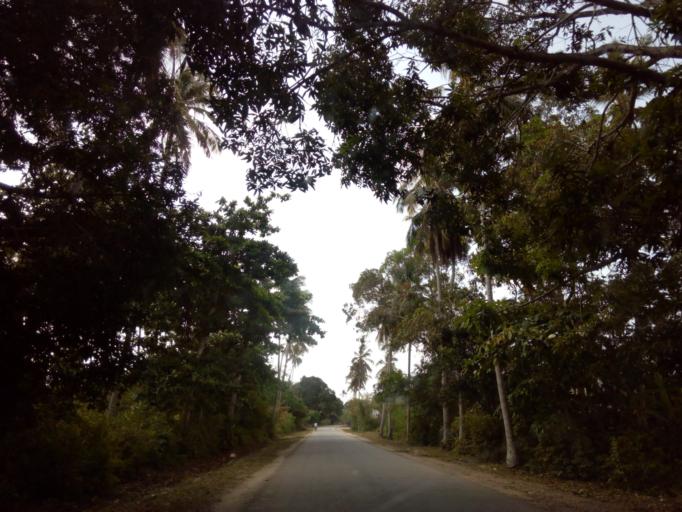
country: TZ
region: Zanzibar Central/South
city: Mahonda
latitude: -6.2948
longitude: 39.3721
